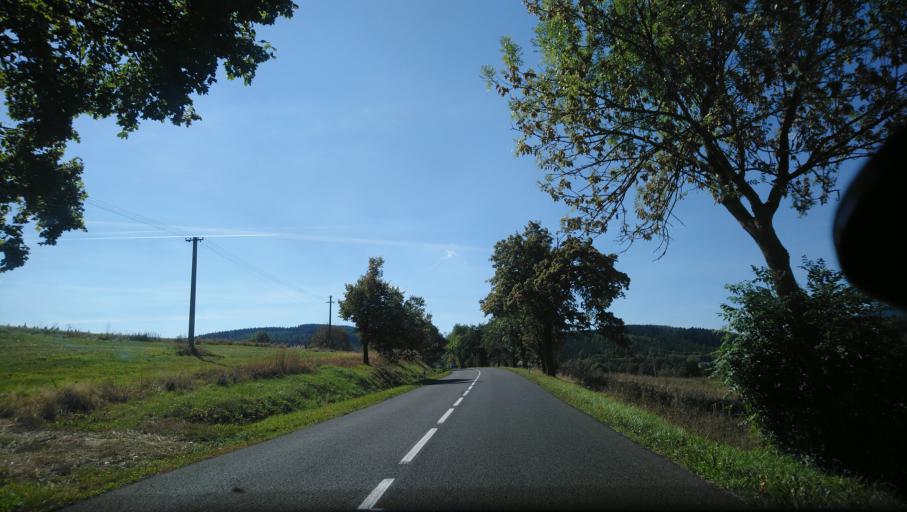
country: CZ
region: Ustecky
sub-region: Okres Chomutov
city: Kovarska
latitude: 50.4439
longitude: 13.0189
